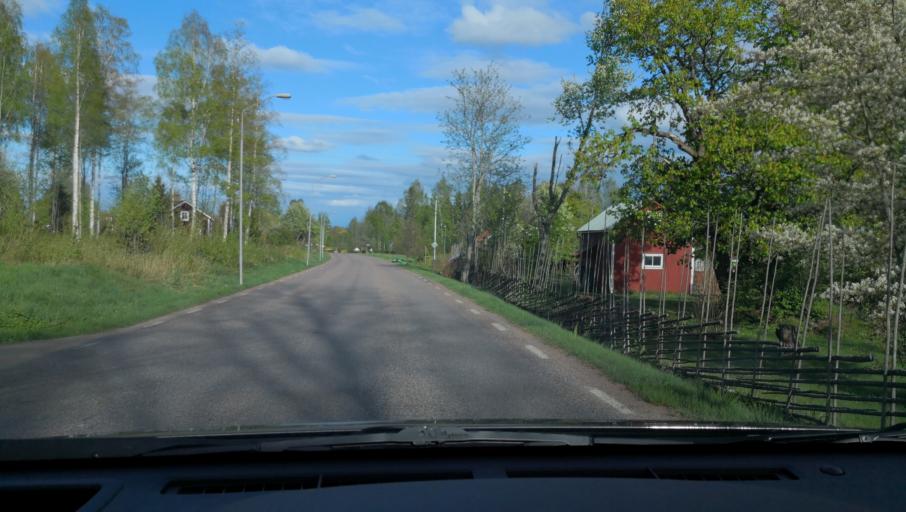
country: SE
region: Dalarna
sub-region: Saters Kommun
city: Saeter
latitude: 60.2993
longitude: 15.8412
